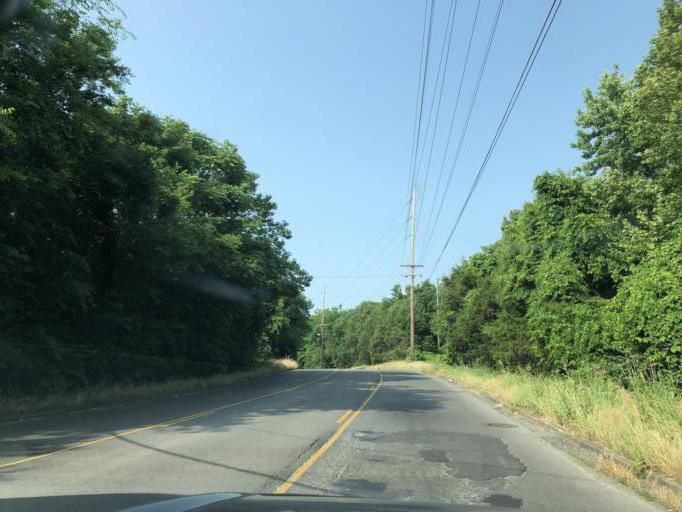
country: US
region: Tennessee
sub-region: Rutherford County
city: La Vergne
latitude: 36.0590
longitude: -86.6350
